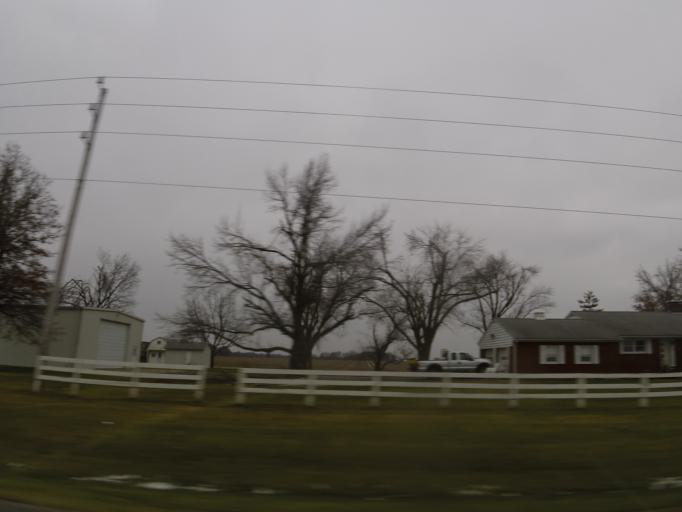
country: US
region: Missouri
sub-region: Marion County
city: Palmyra
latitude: 39.7437
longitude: -91.4752
